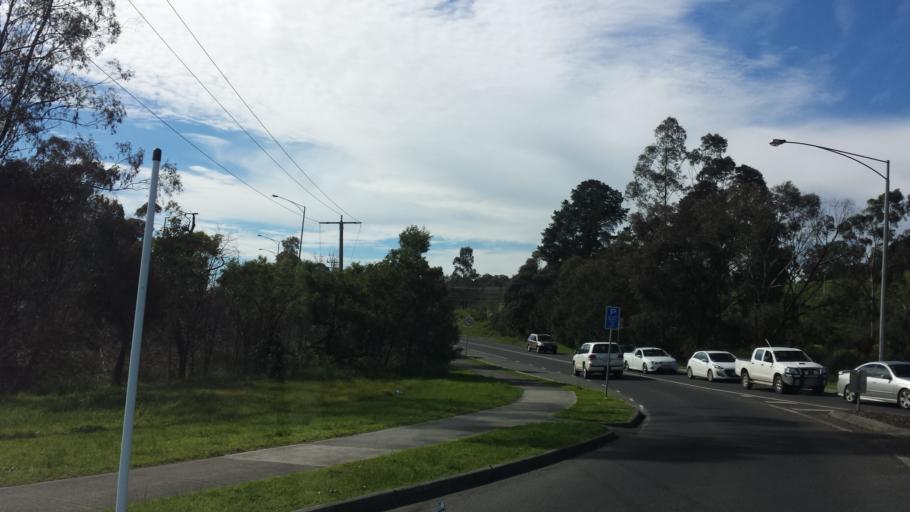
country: AU
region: Victoria
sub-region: Nillumbik
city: Wattleglen
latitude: -37.6659
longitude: 145.1813
